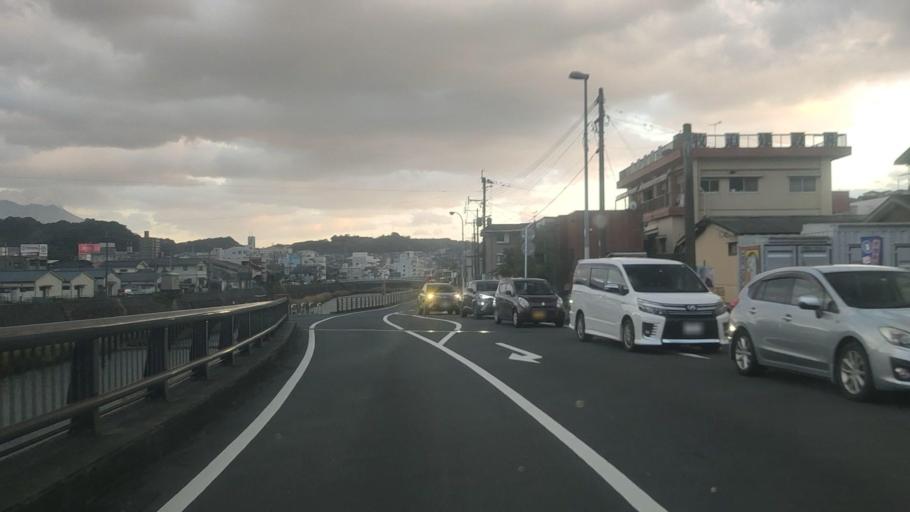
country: JP
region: Kagoshima
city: Kagoshima-shi
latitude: 31.6131
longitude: 130.5288
